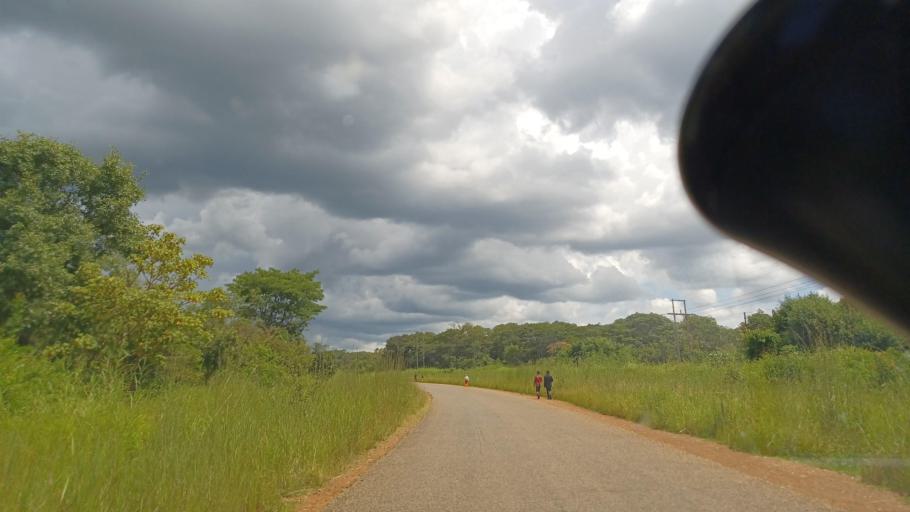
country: ZM
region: North-Western
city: Kasempa
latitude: -12.7785
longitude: 26.0096
